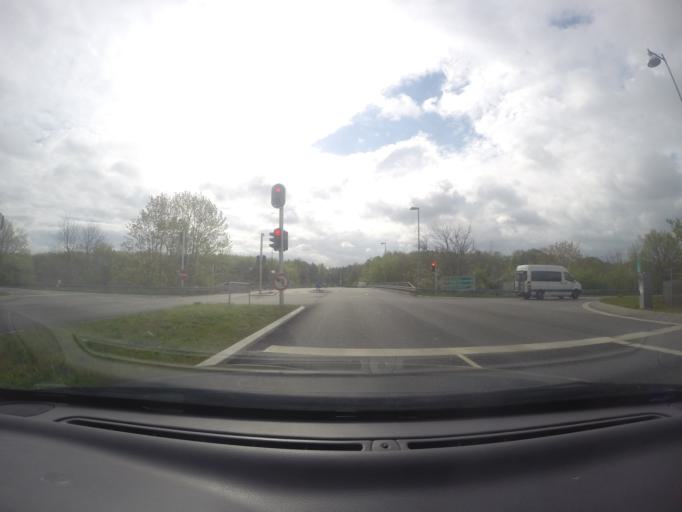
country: DK
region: Capital Region
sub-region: Albertslund Kommune
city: Albertslund
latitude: 55.6836
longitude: 12.3336
